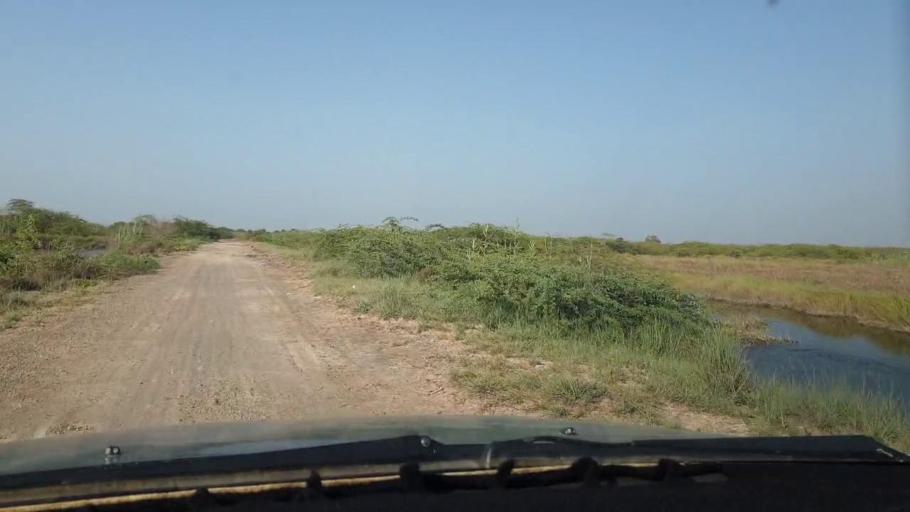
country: PK
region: Sindh
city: Chambar
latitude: 25.2664
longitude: 68.9280
